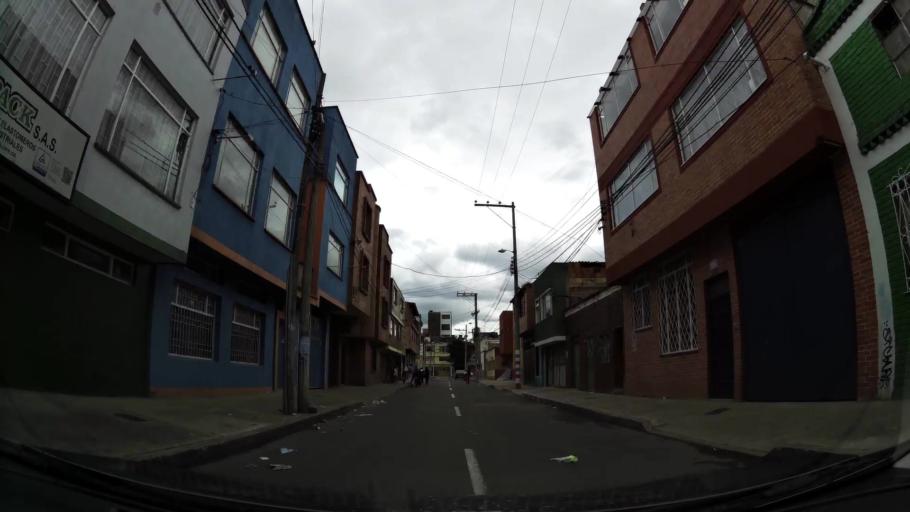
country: CO
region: Bogota D.C.
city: Barrio San Luis
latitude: 4.6958
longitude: -74.0957
